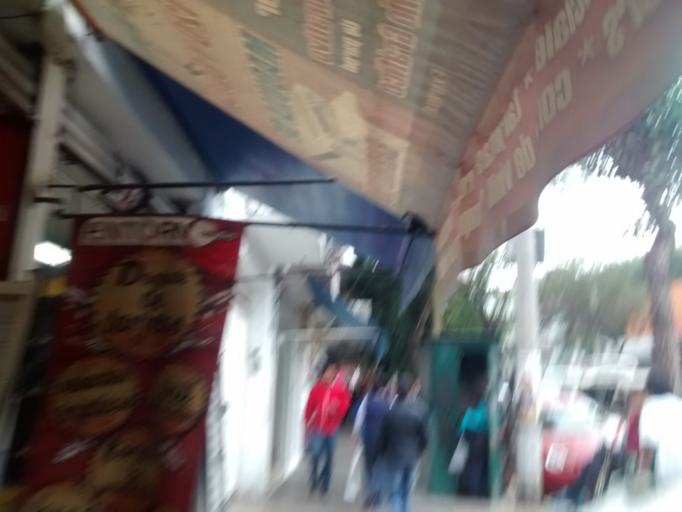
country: MX
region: Mexico City
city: Benito Juarez
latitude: 19.4071
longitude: -99.1395
